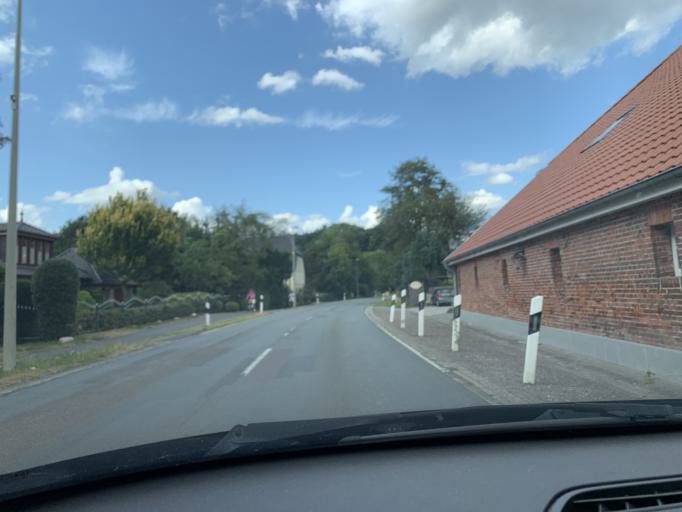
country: DE
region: Lower Saxony
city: Bad Zwischenahn
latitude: 53.1936
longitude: 8.0431
